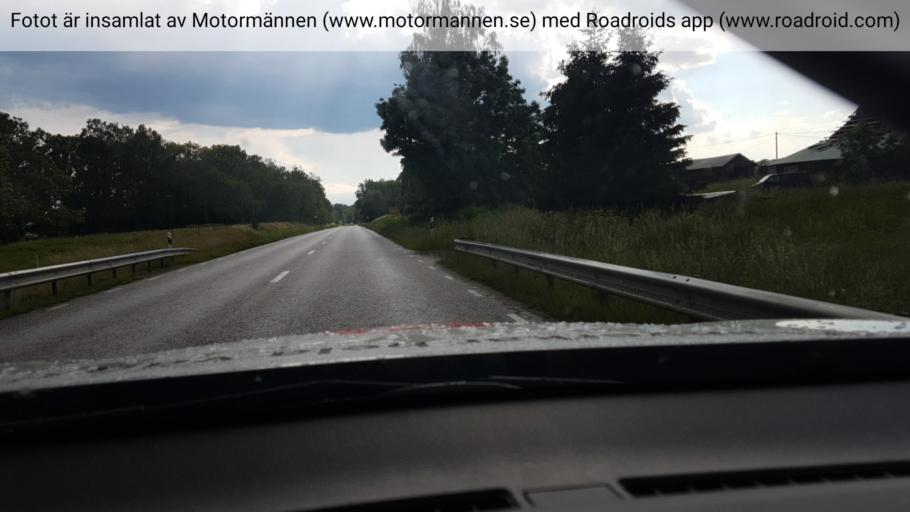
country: SE
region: Vaestra Goetaland
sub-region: Hjo Kommun
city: Hjo
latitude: 58.2327
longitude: 14.2183
